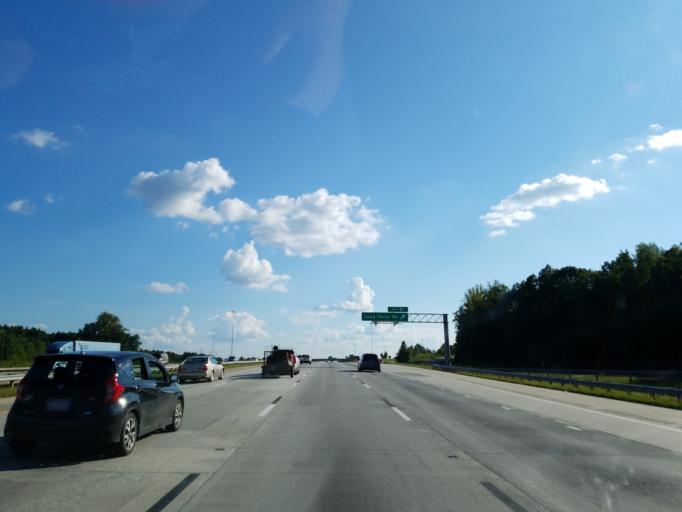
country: US
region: North Carolina
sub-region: Rowan County
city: Spencer
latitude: 35.6990
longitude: -80.4000
